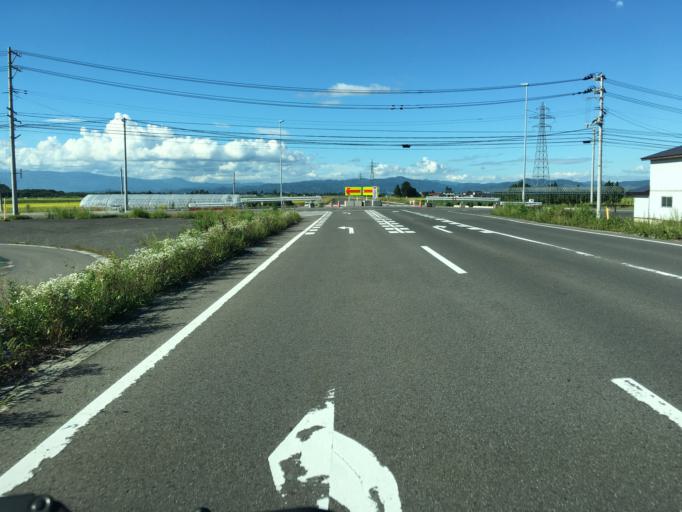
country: JP
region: Yamagata
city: Yonezawa
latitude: 37.9551
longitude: 140.1126
